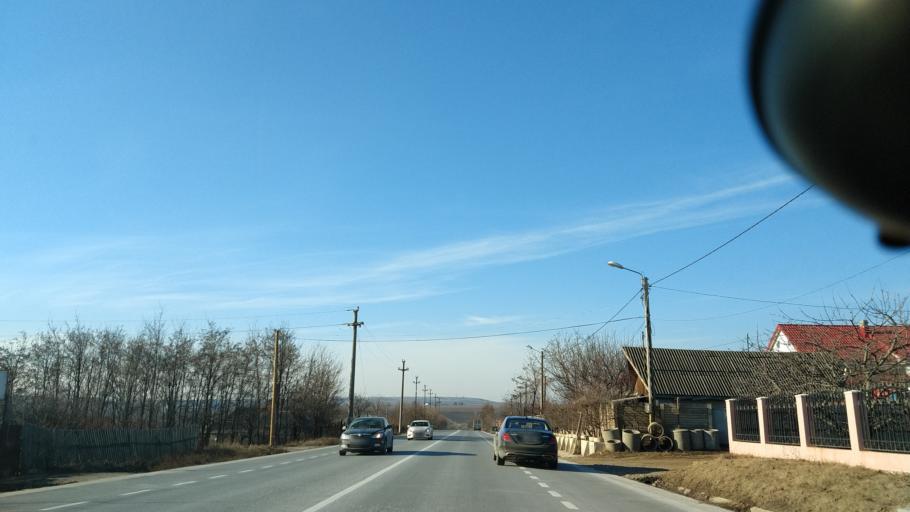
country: RO
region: Iasi
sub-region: Comuna Lungani
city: Zmeu
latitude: 47.2248
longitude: 27.1871
